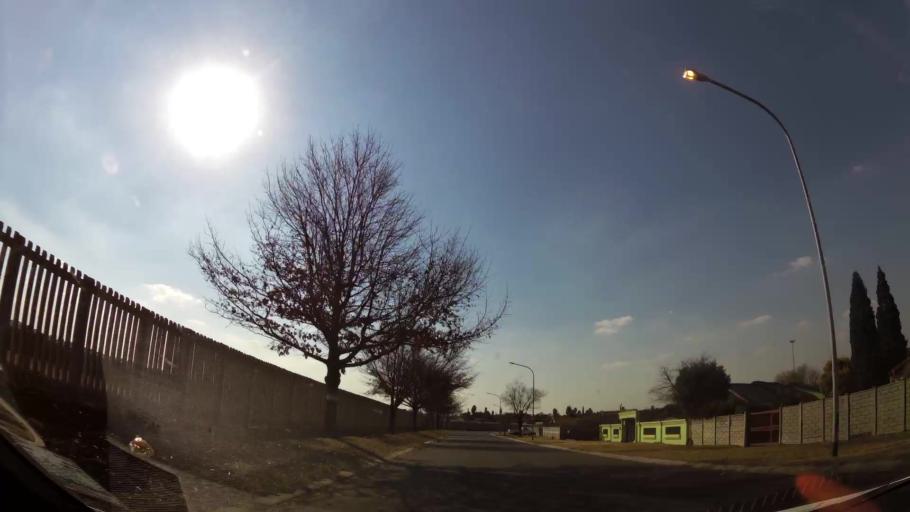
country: ZA
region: Gauteng
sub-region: Ekurhuleni Metropolitan Municipality
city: Benoni
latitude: -26.2417
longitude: 28.3071
